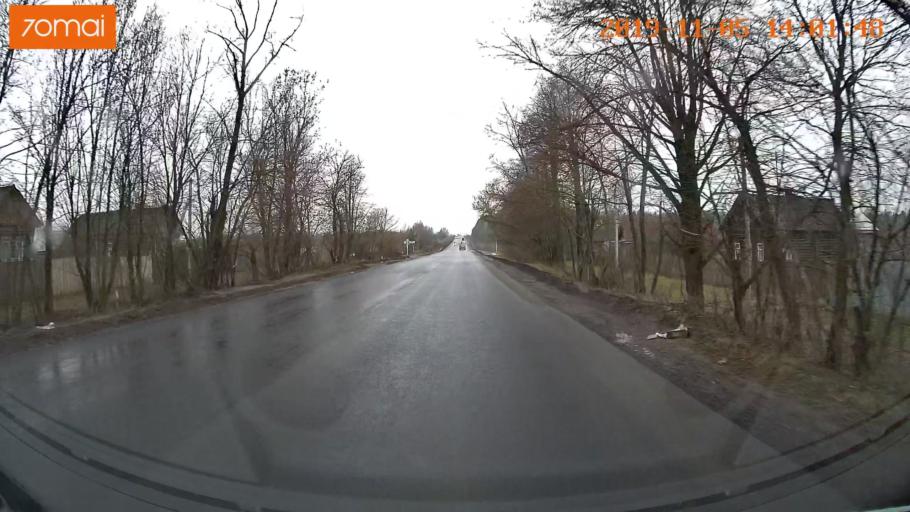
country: RU
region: Ivanovo
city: Kokhma
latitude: 57.0066
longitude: 41.2245
